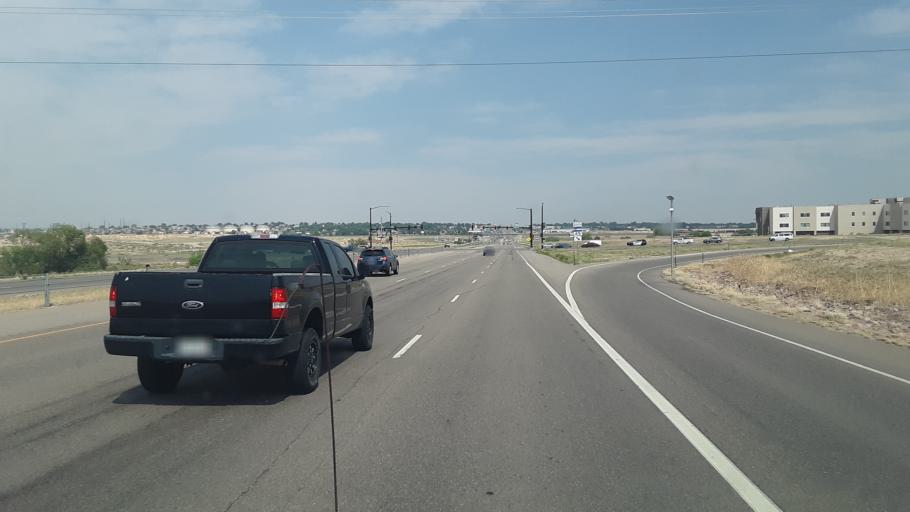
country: US
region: Colorado
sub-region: Pueblo County
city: Pueblo West
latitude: 38.3143
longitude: -104.6635
